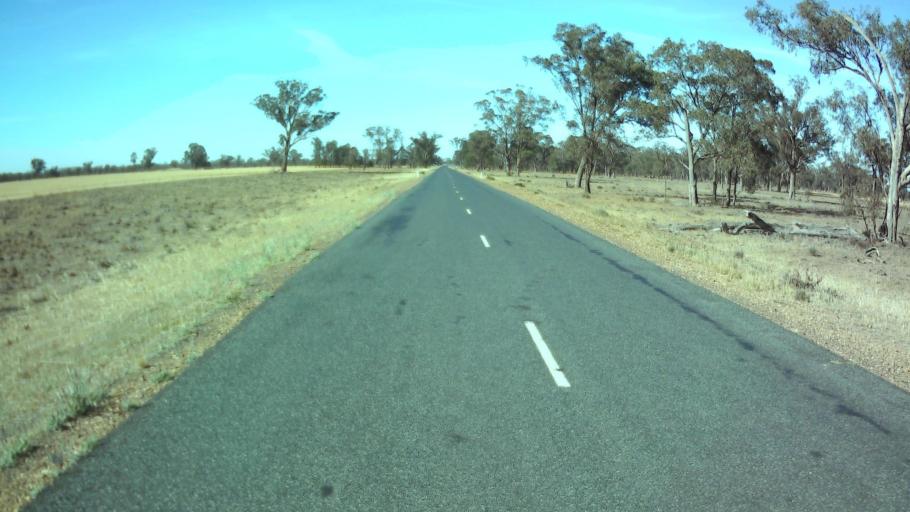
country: AU
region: New South Wales
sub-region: Weddin
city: Grenfell
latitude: -34.0877
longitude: 147.8911
